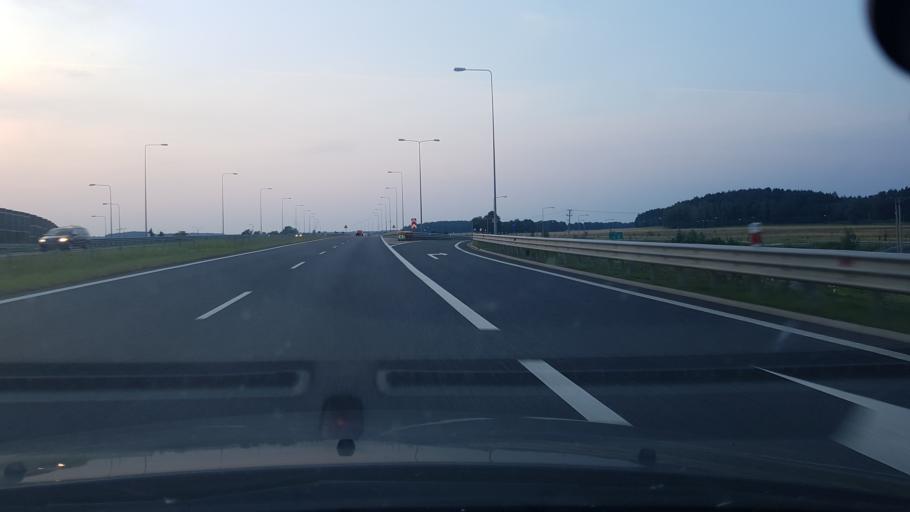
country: PL
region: Warmian-Masurian Voivodeship
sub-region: Powiat nidzicki
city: Nidzica
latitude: 53.4094
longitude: 20.3393
